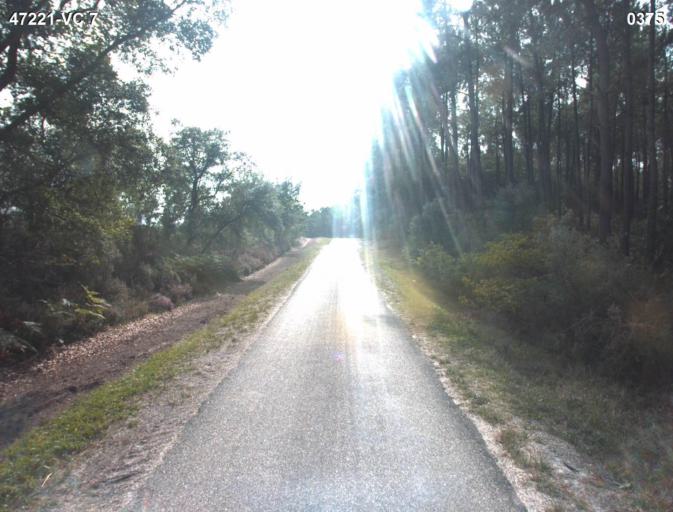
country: FR
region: Aquitaine
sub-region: Departement du Lot-et-Garonne
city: Mezin
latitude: 44.0963
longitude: 0.2253
